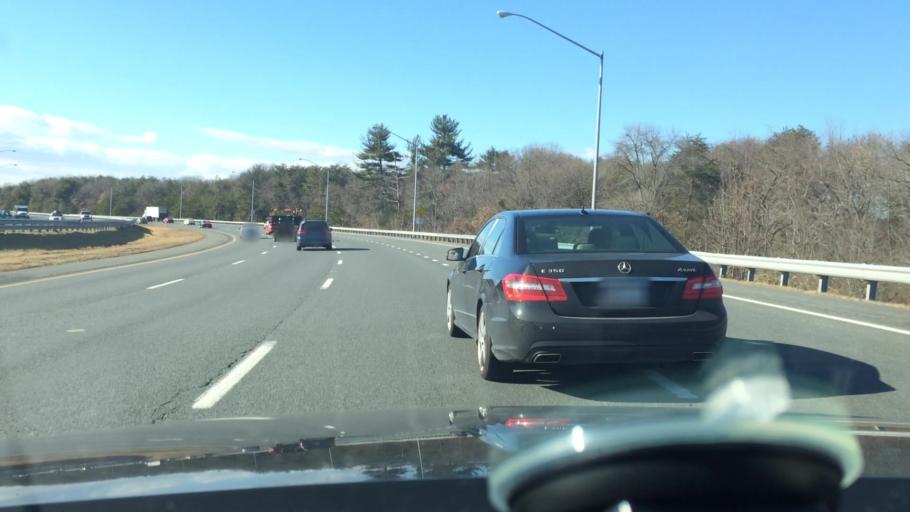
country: US
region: Maryland
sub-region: Anne Arundel County
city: Glen Burnie
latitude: 39.1572
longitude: -76.6530
